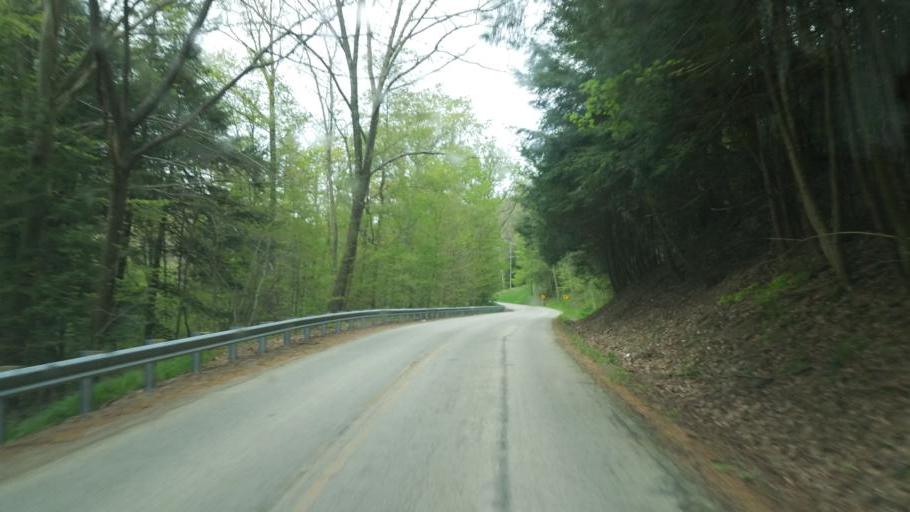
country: US
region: Ohio
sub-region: Ashland County
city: Loudonville
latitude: 40.6240
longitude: -82.3212
